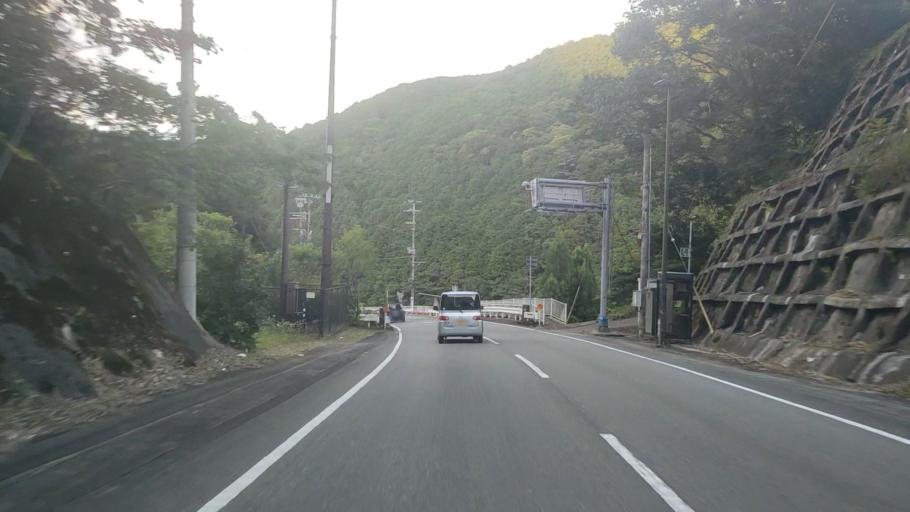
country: JP
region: Wakayama
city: Tanabe
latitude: 33.7817
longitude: 135.5055
